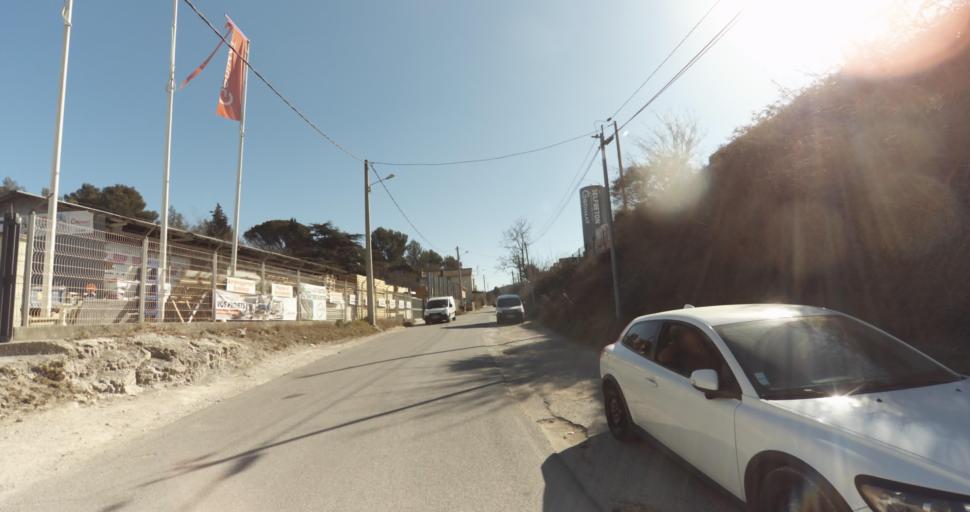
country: FR
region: Provence-Alpes-Cote d'Azur
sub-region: Departement des Bouches-du-Rhone
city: Cadolive
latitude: 43.4000
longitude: 5.5630
